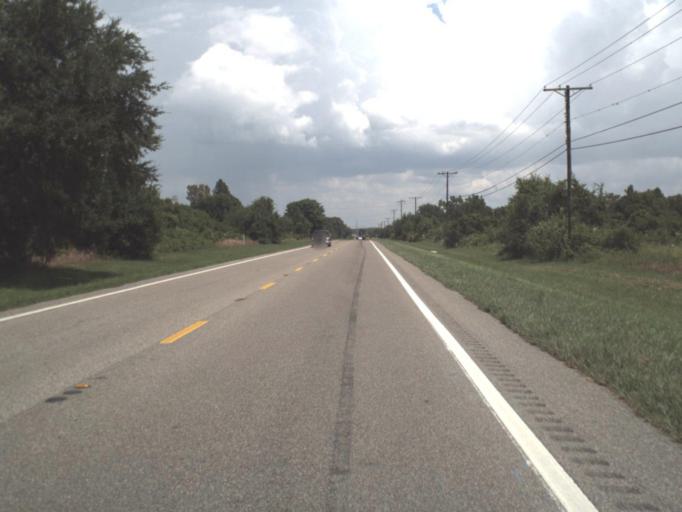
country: US
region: Florida
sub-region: Hillsborough County
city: Sun City Center
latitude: 27.7018
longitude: -82.3386
